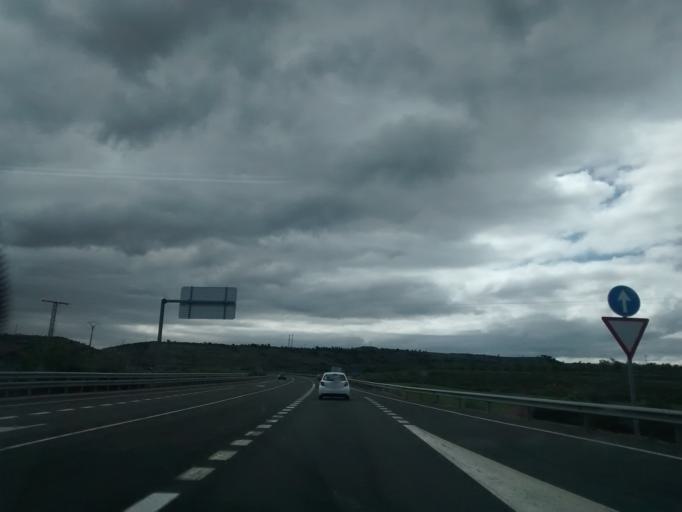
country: ES
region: La Rioja
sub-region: Provincia de La Rioja
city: Ausejo
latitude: 42.3431
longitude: -2.1775
